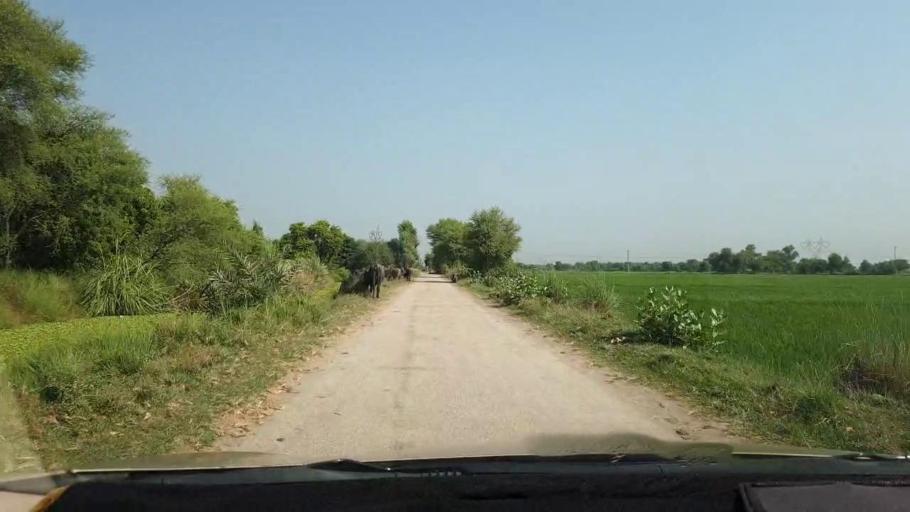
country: PK
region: Sindh
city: Larkana
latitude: 27.6349
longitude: 68.2372
